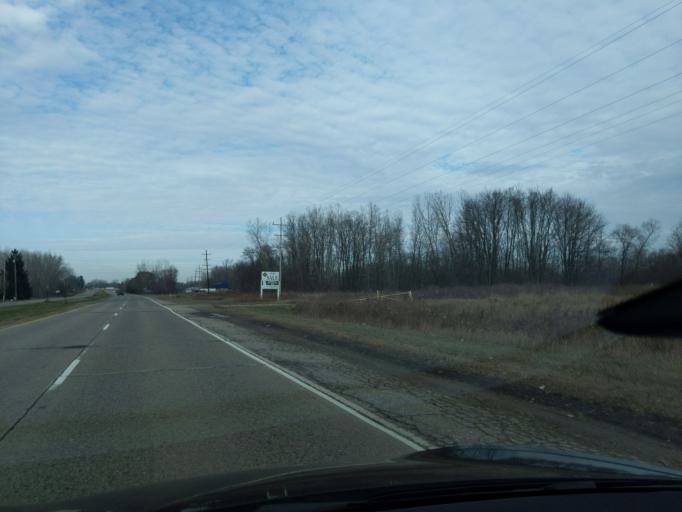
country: US
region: Michigan
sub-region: Ingham County
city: Holt
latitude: 42.6257
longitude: -84.5024
